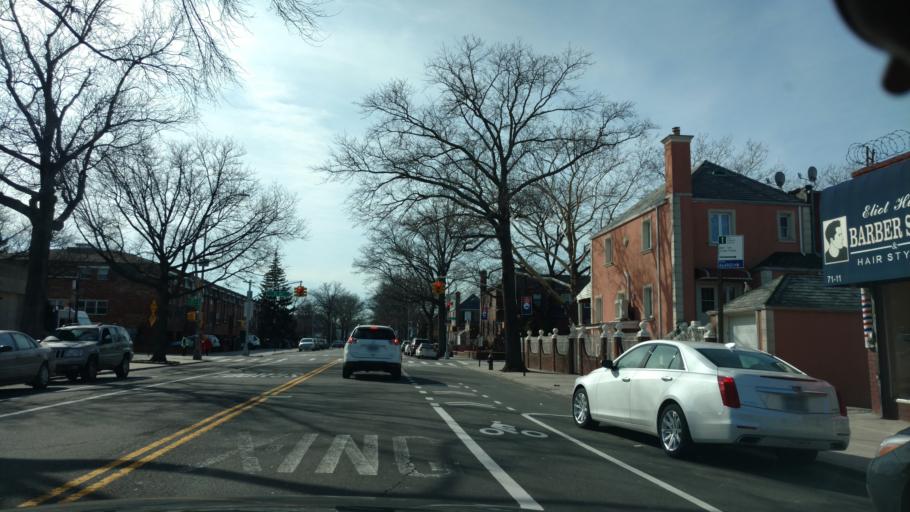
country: US
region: New York
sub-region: Kings County
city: East New York
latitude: 40.7216
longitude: -73.8867
